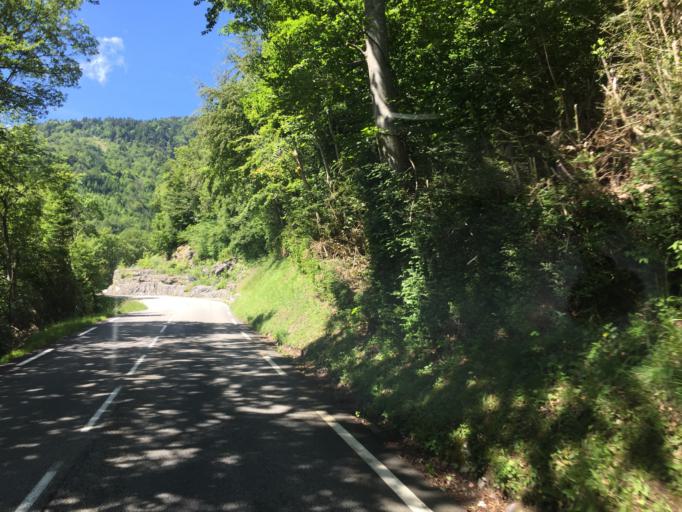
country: FR
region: Rhone-Alpes
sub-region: Departement de la Savoie
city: Saint-Baldoph
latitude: 45.5037
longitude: 5.9190
